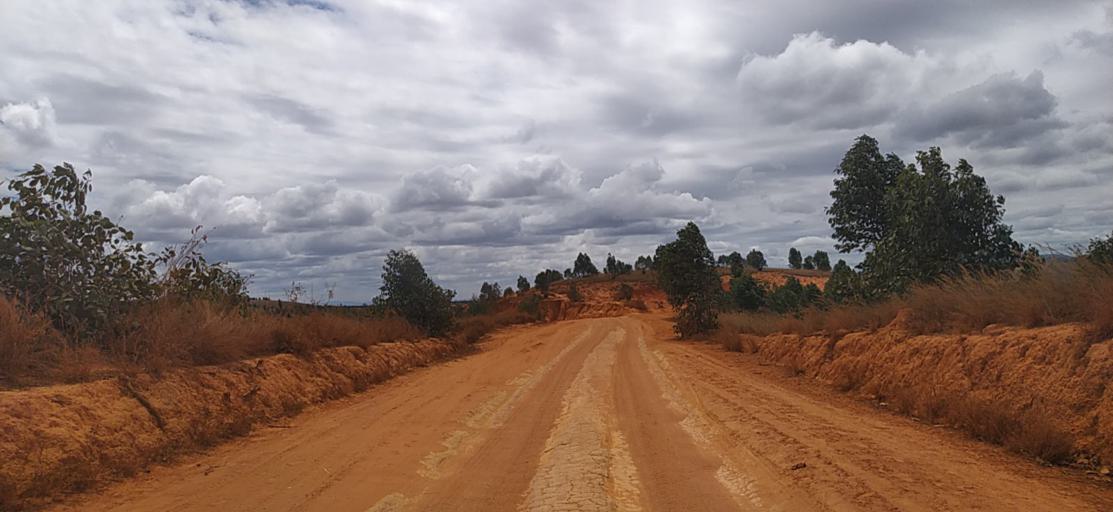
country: MG
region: Alaotra Mangoro
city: Ambatondrazaka
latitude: -18.0621
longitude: 48.2571
